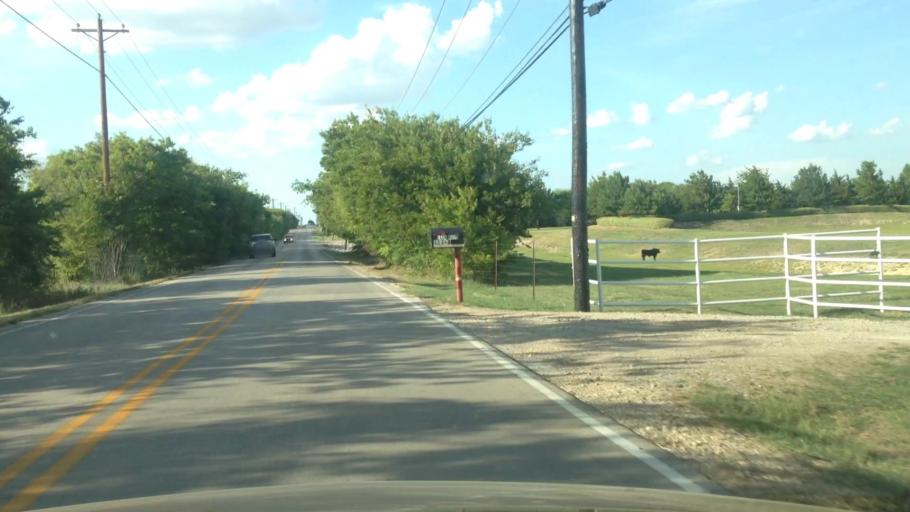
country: US
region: Texas
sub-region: Tarrant County
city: Haslet
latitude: 32.9327
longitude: -97.3920
